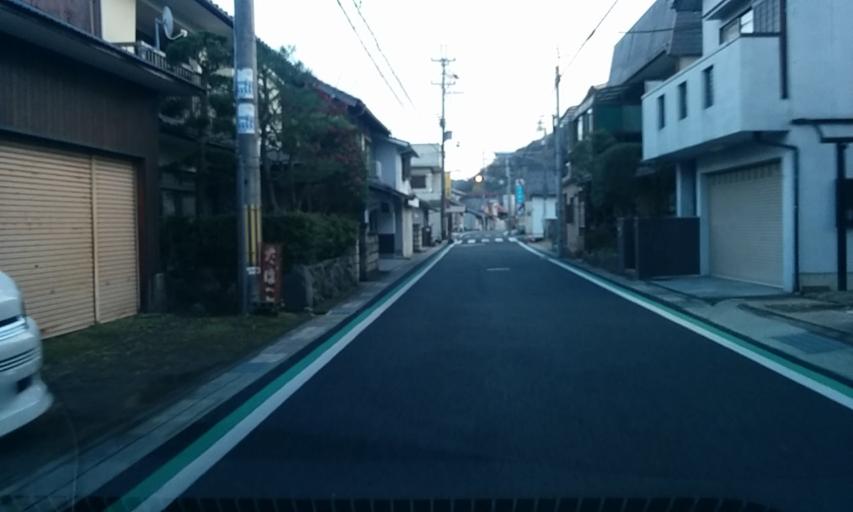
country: JP
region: Kyoto
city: Kameoka
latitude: 35.1566
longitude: 135.4254
